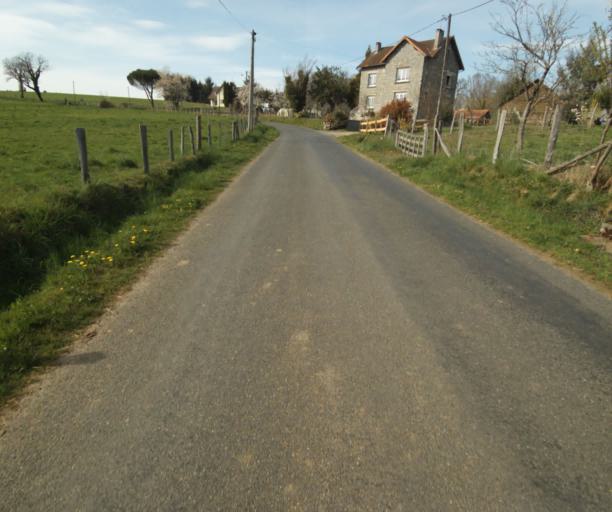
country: FR
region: Limousin
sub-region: Departement de la Correze
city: Naves
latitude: 45.3298
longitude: 1.7332
